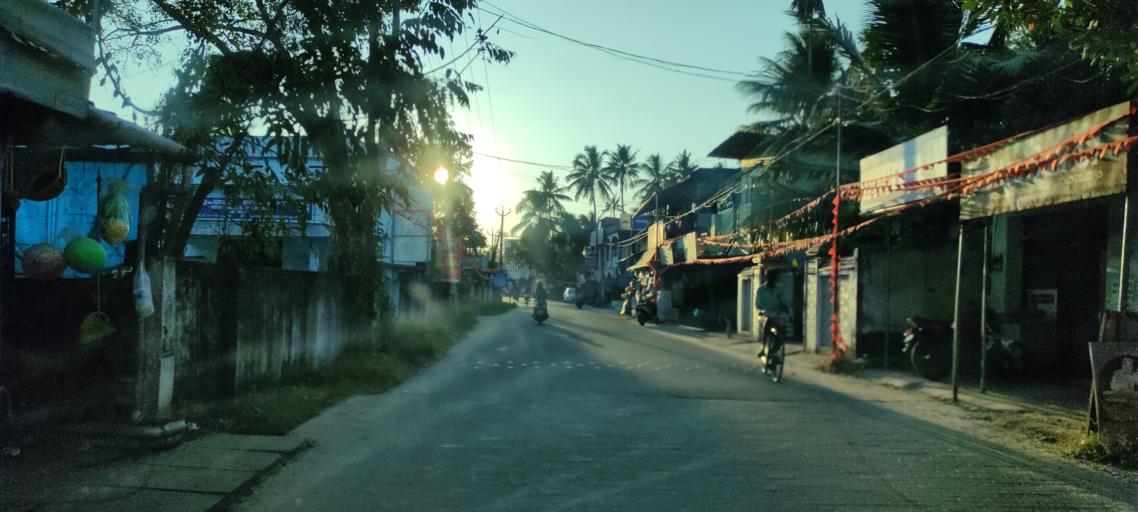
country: IN
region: Kerala
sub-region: Alappuzha
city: Kayankulam
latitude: 9.1902
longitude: 76.4710
